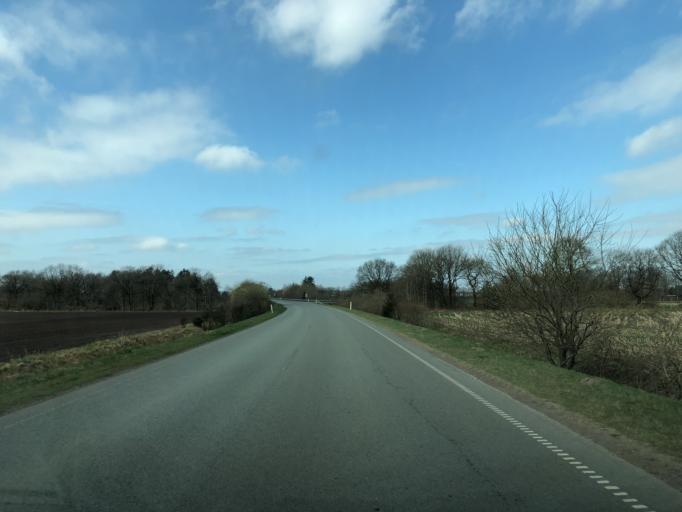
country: DK
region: Central Jutland
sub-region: Ikast-Brande Kommune
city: Brande
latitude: 55.9286
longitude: 9.1744
